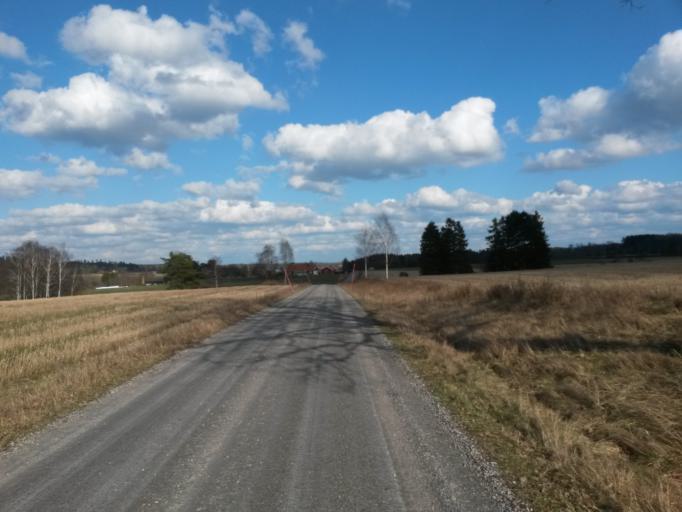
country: SE
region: Vaestra Goetaland
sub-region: Vargarda Kommun
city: Jonstorp
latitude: 57.9895
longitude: 12.6450
